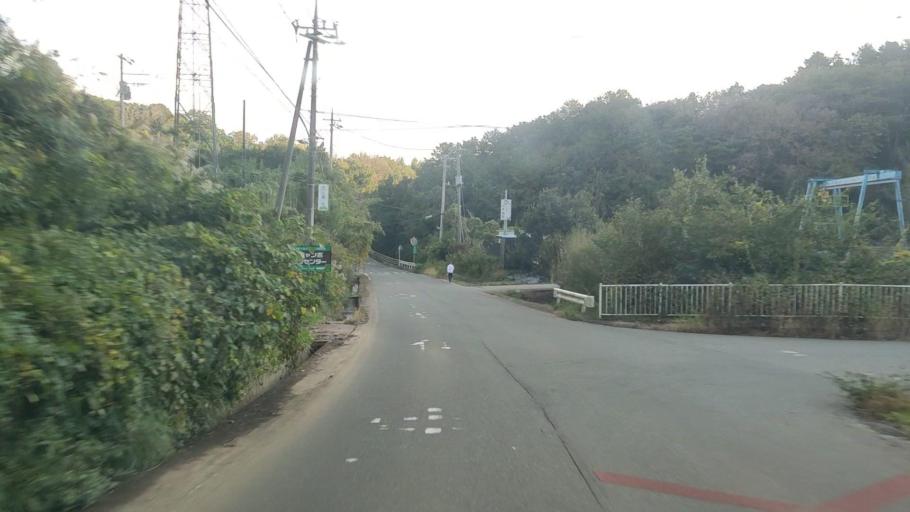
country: JP
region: Shizuoka
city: Mishima
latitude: 35.1433
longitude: 138.9438
